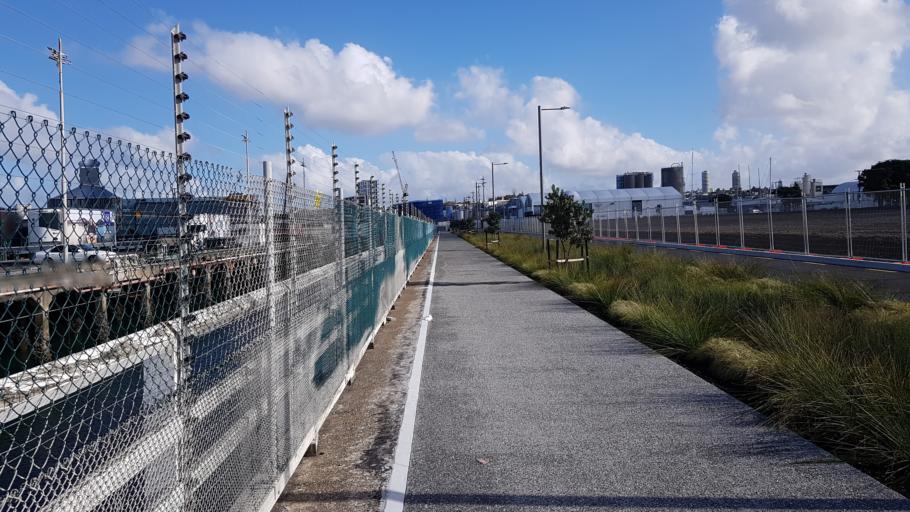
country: NZ
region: Auckland
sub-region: Auckland
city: Auckland
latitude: -36.8371
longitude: 174.7594
